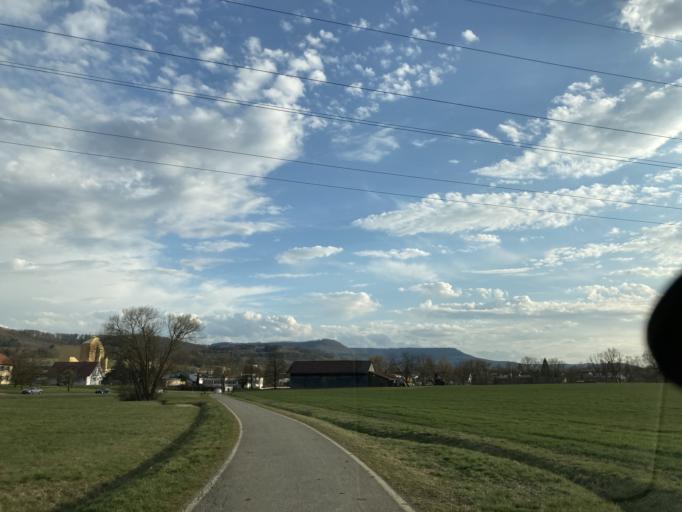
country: DE
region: Baden-Wuerttemberg
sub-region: Tuebingen Region
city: Nehren
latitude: 48.4388
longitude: 9.0783
